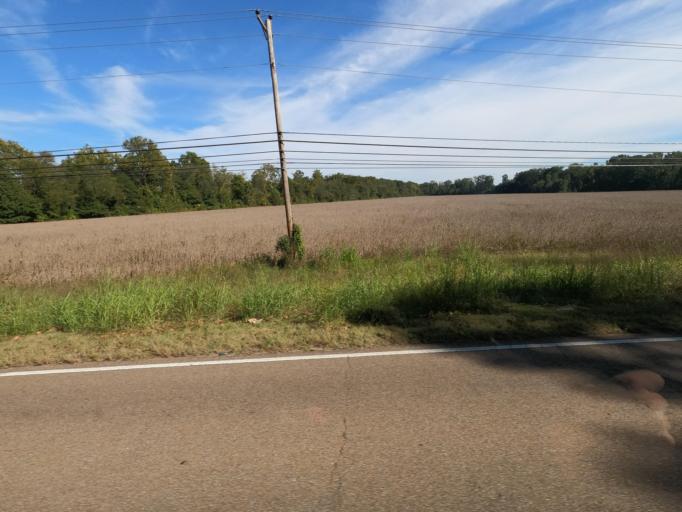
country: US
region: Tennessee
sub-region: Fayette County
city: Hickory Withe
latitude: 35.2207
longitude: -89.6503
